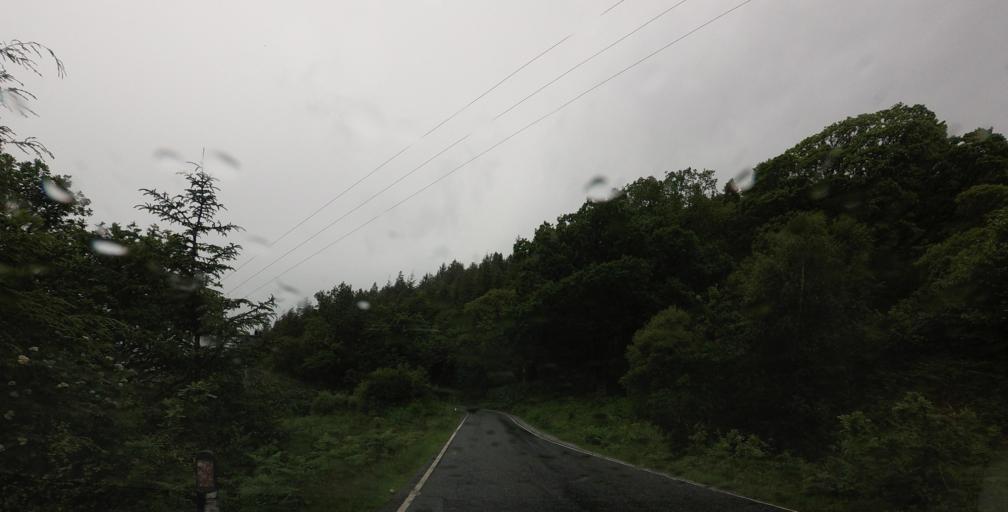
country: GB
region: Scotland
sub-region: Argyll and Bute
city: Isle Of Mull
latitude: 56.6855
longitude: -5.6466
